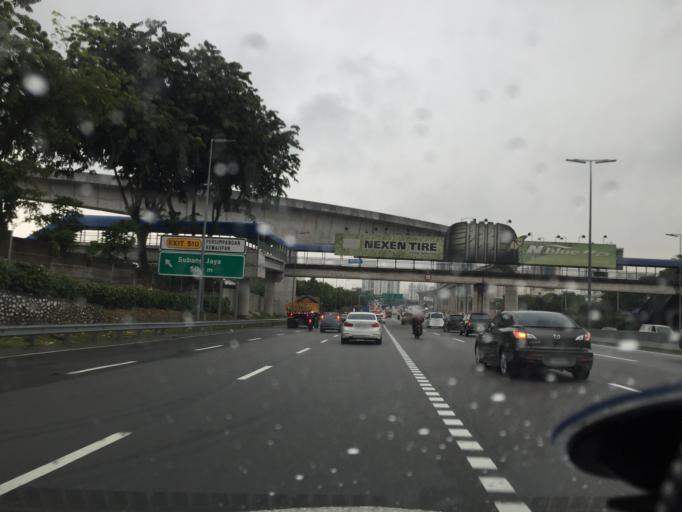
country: MY
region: Selangor
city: Subang Jaya
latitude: 3.0633
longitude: 101.5854
